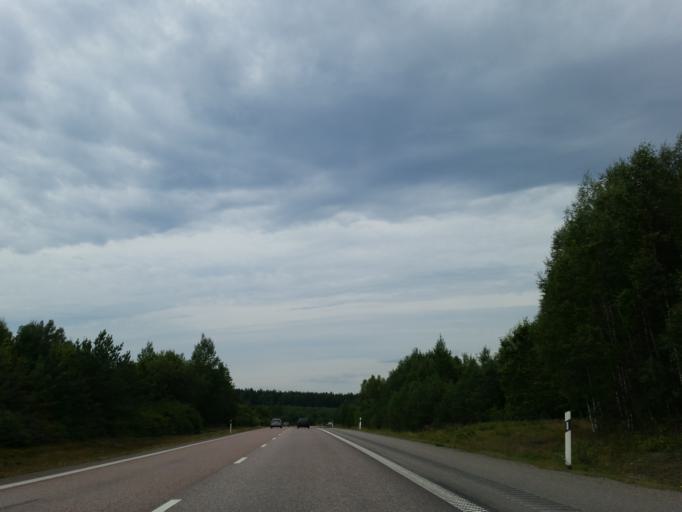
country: SE
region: Soedermanland
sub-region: Strangnas Kommun
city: Mariefred
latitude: 59.2253
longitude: 17.2455
